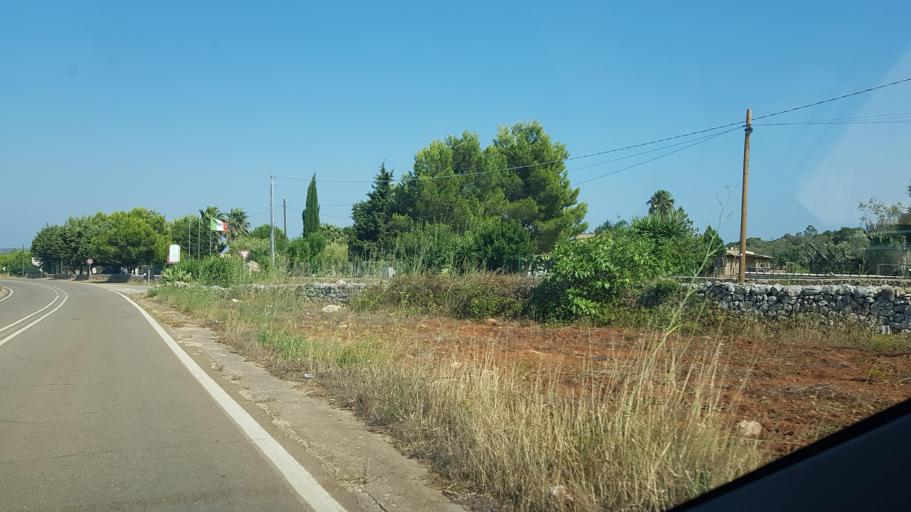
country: IT
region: Apulia
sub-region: Provincia di Lecce
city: Gemini
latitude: 39.8670
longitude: 18.2132
